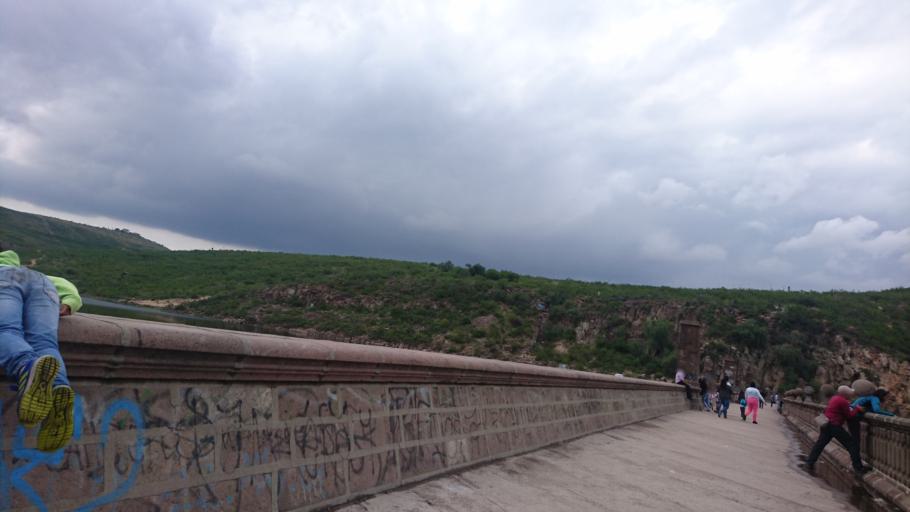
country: MX
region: San Luis Potosi
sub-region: Mexquitic de Carmona
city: Guadalupe Victoria
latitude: 22.1500
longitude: -101.0544
